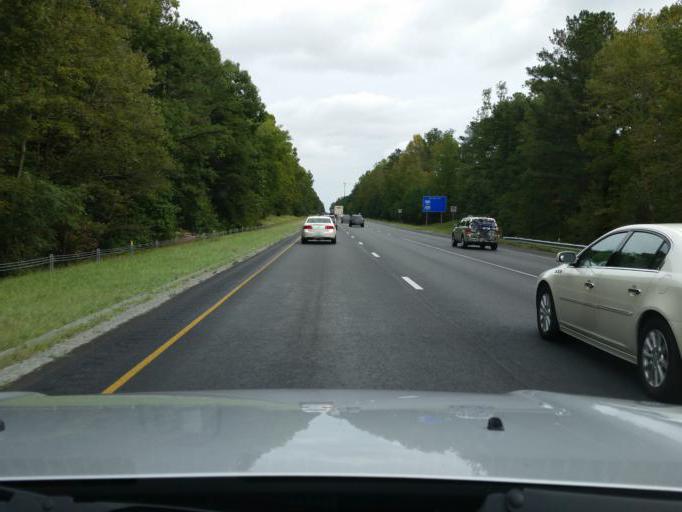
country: US
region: Virginia
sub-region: New Kent County
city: New Kent
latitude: 37.4971
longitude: -77.0395
